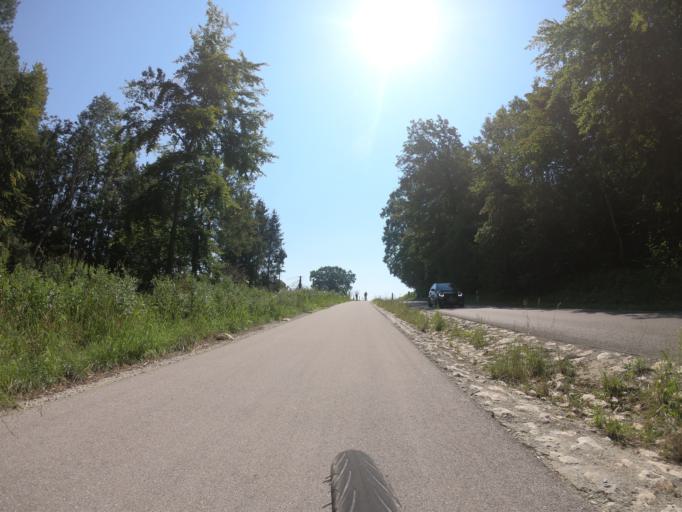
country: DE
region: Bavaria
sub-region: Upper Bavaria
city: Fuerstenfeldbruck
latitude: 48.1595
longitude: 11.2565
